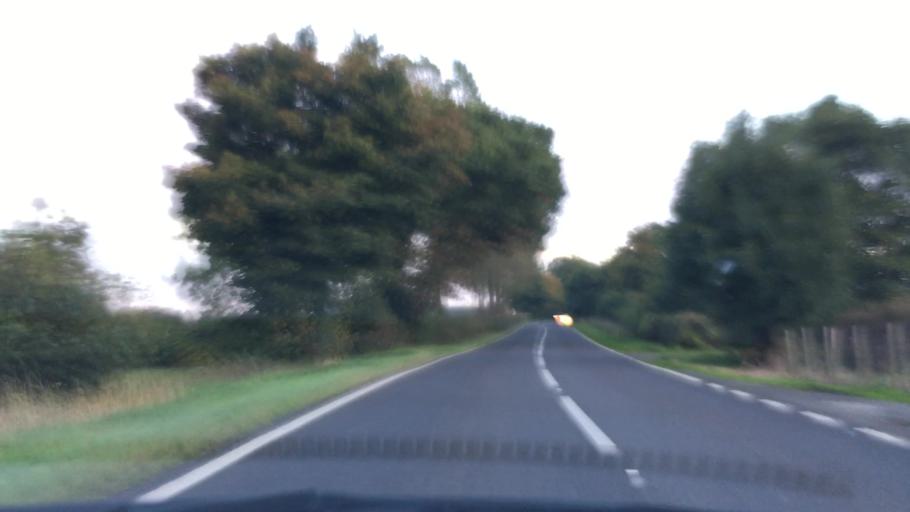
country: GB
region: England
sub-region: North East Lincolnshire
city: Wold Newton
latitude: 53.4625
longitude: -0.0973
